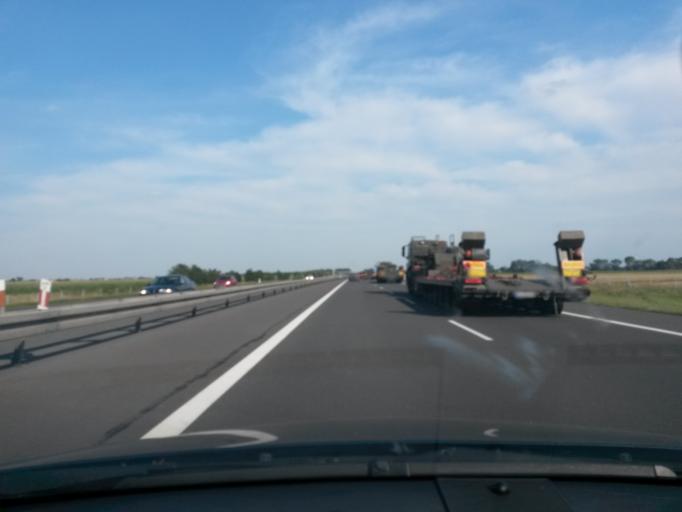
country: PL
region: Greater Poland Voivodeship
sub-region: Powiat wrzesinski
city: Wrzesnia
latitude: 52.2983
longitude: 17.6355
